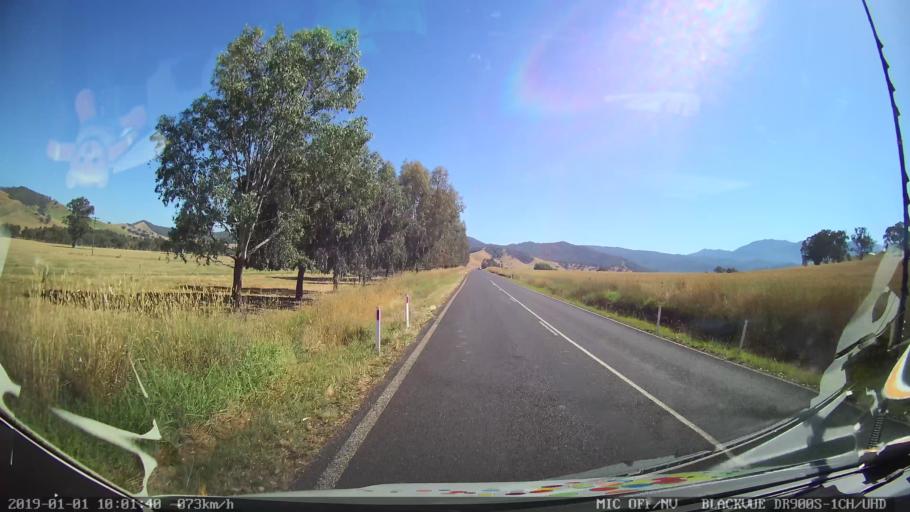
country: AU
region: New South Wales
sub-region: Snowy River
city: Jindabyne
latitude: -36.1892
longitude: 148.1006
